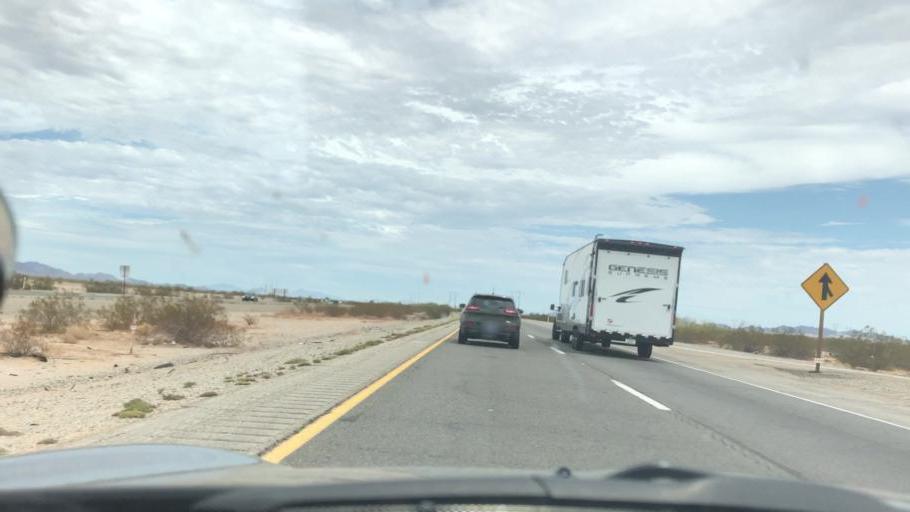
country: US
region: California
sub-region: Riverside County
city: Mesa Verde
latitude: 33.6072
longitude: -114.9881
